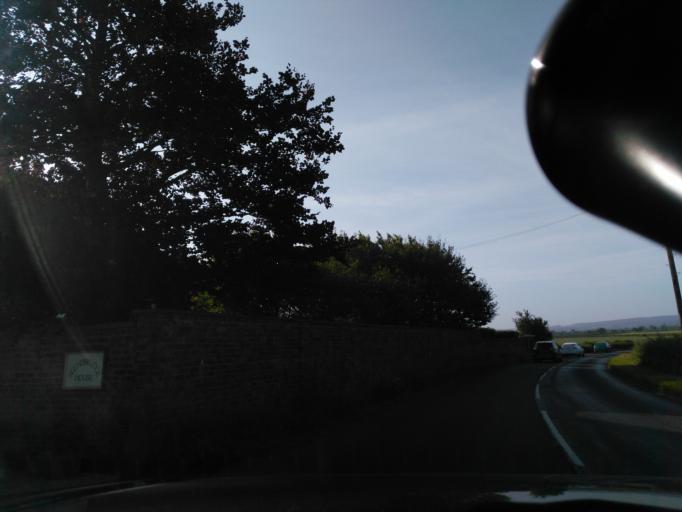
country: GB
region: England
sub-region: Wiltshire
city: Seend
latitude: 51.3373
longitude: -2.0804
